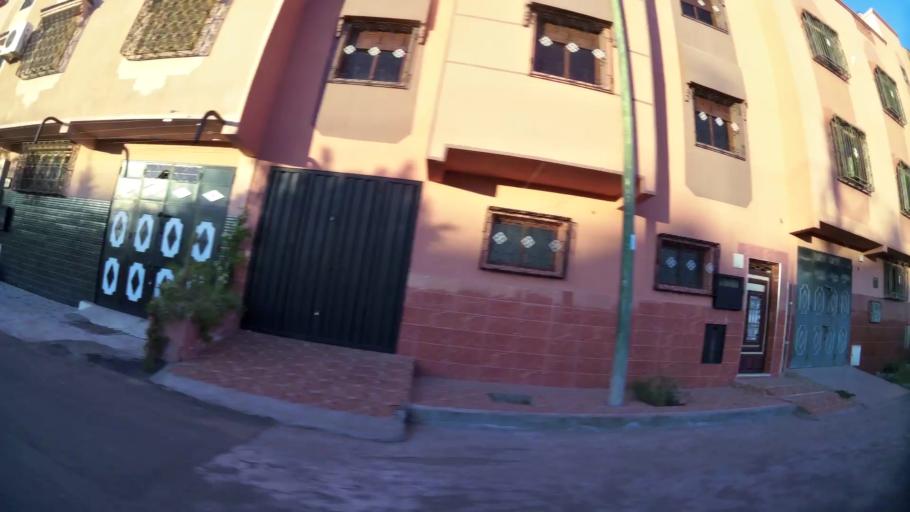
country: MA
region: Marrakech-Tensift-Al Haouz
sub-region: Marrakech
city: Marrakesh
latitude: 31.6360
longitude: -8.0374
